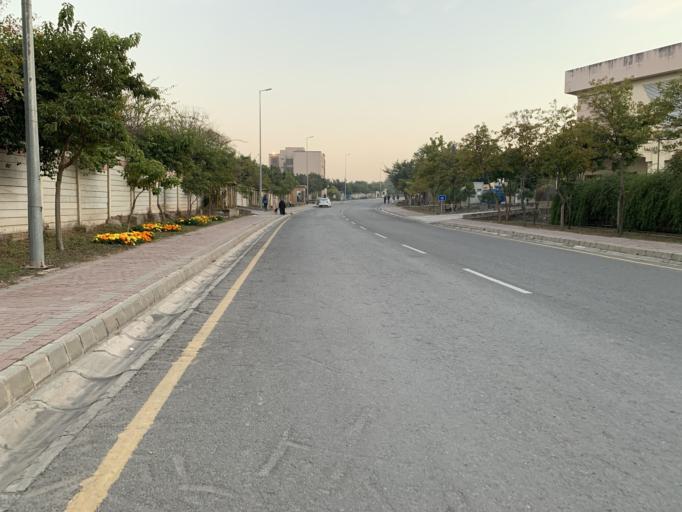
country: PK
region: Punjab
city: Rawalpindi
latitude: 33.6454
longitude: 72.9934
